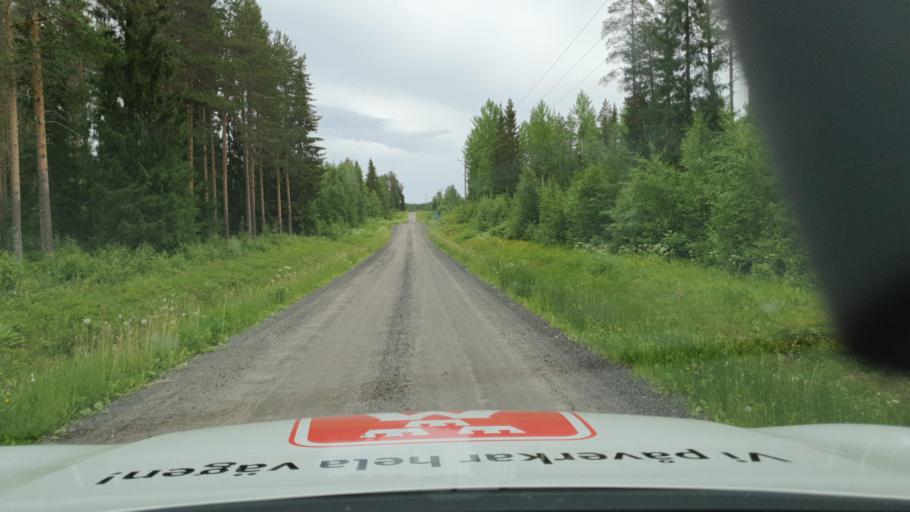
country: SE
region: Vaesterbotten
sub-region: Skelleftea Kommun
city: Burtraesk
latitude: 64.3461
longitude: 20.6059
